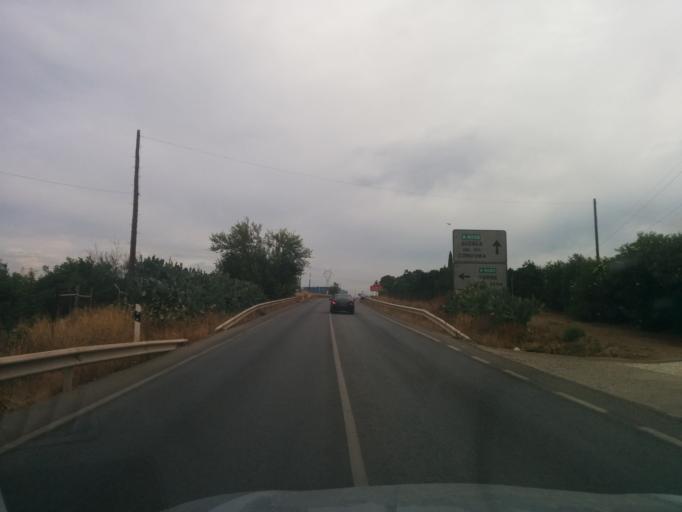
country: ES
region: Andalusia
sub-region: Provincia de Sevilla
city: La Rinconada
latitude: 37.4947
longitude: -6.0105
